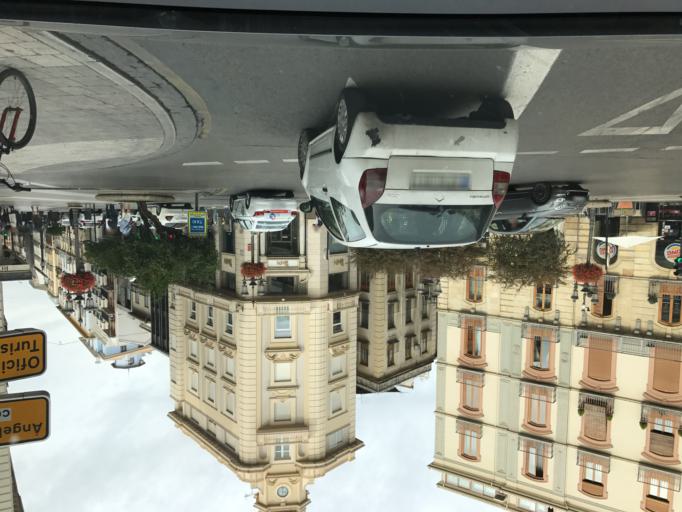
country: ES
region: Andalusia
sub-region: Provincia de Granada
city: Granada
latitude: 37.1732
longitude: -3.5996
